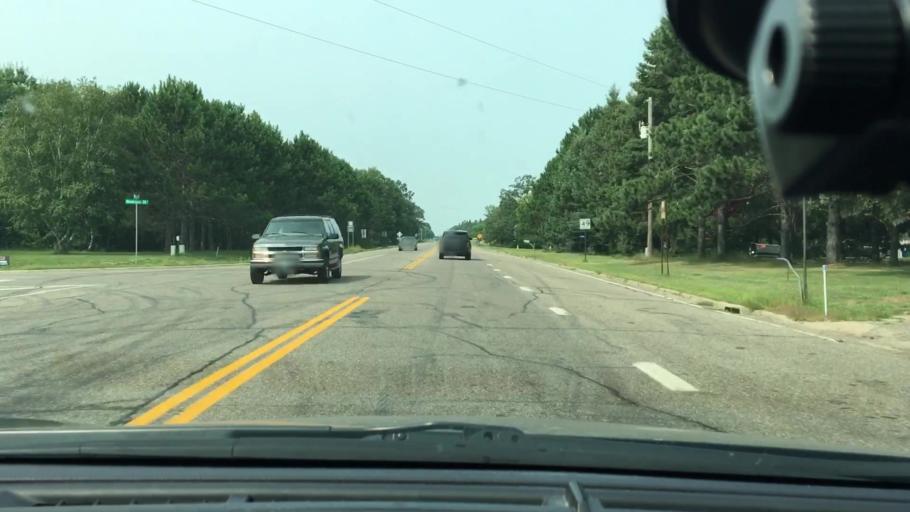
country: US
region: Minnesota
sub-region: Crow Wing County
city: Brainerd
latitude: 46.3988
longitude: -94.1784
